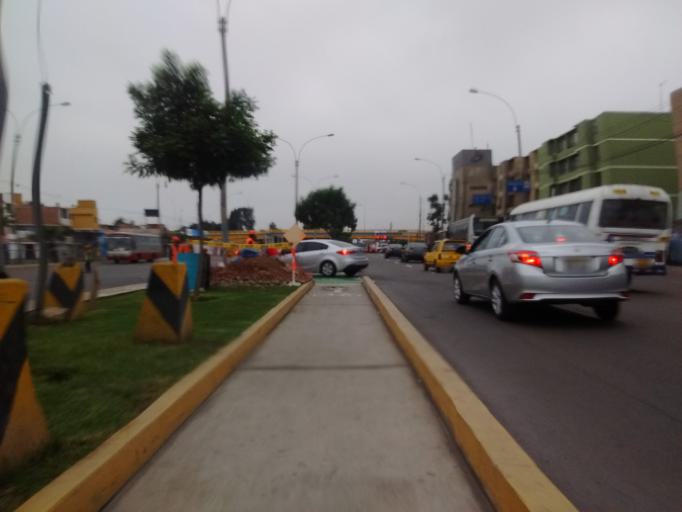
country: PE
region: Callao
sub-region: Callao
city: Callao
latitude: -12.0623
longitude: -77.0786
